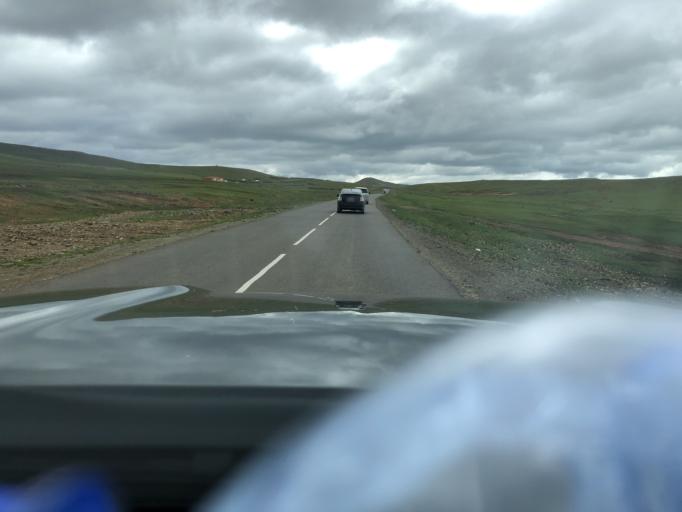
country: MN
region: Central Aimak
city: Ihsueuej
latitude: 48.0203
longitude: 106.5486
